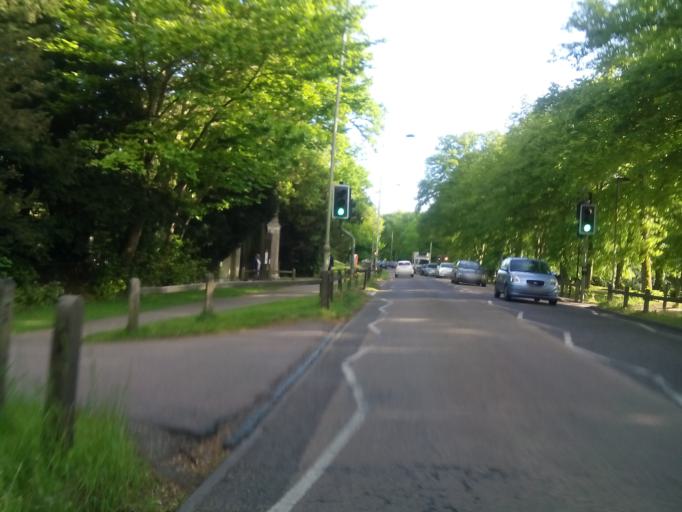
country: GB
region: England
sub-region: Cambridgeshire
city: Cambridge
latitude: 52.2045
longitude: 0.1114
